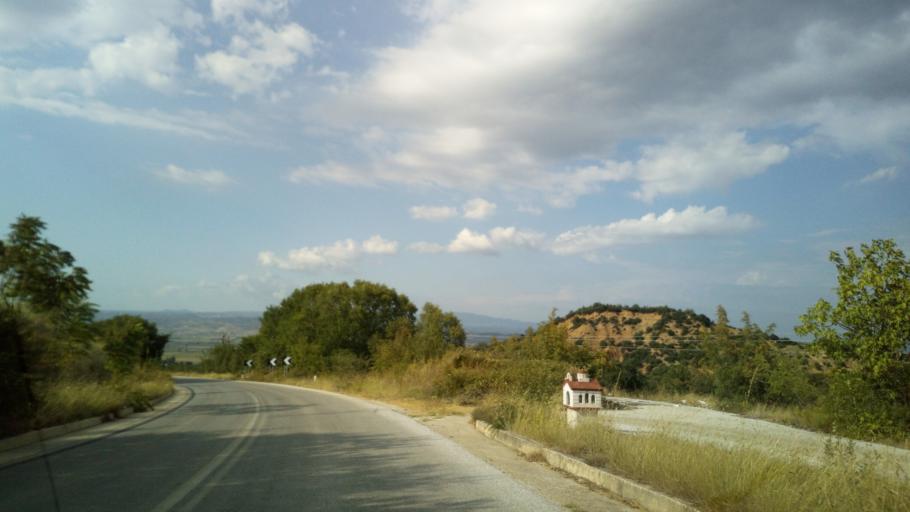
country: GR
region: Central Macedonia
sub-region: Nomos Thessalonikis
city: Gerakarou
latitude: 40.6161
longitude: 23.2235
